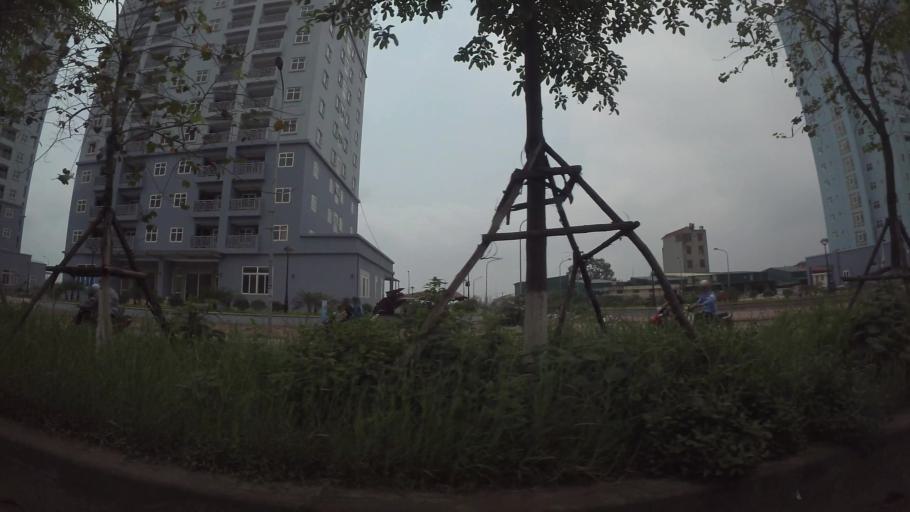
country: VN
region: Ha Noi
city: Hai BaTrung
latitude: 20.9836
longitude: 105.8565
